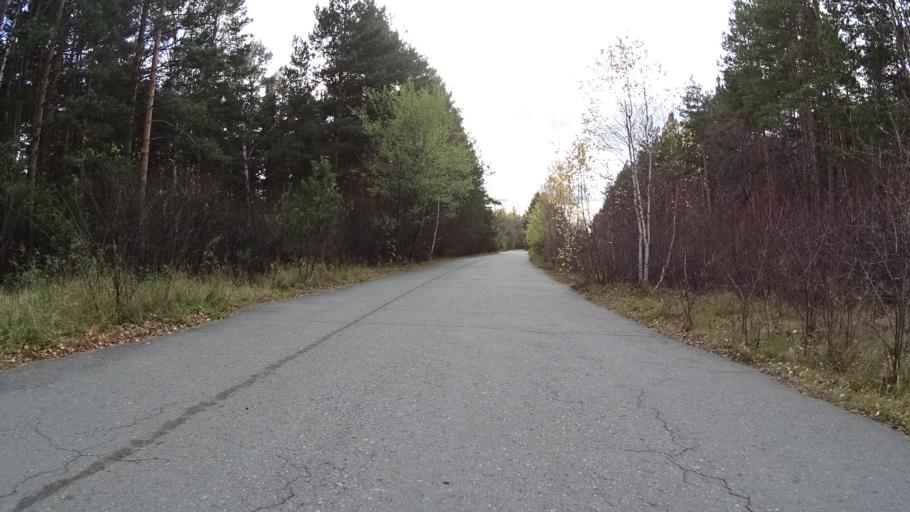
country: RU
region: Chelyabinsk
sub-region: Gorod Chelyabinsk
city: Chelyabinsk
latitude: 55.1547
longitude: 61.3473
